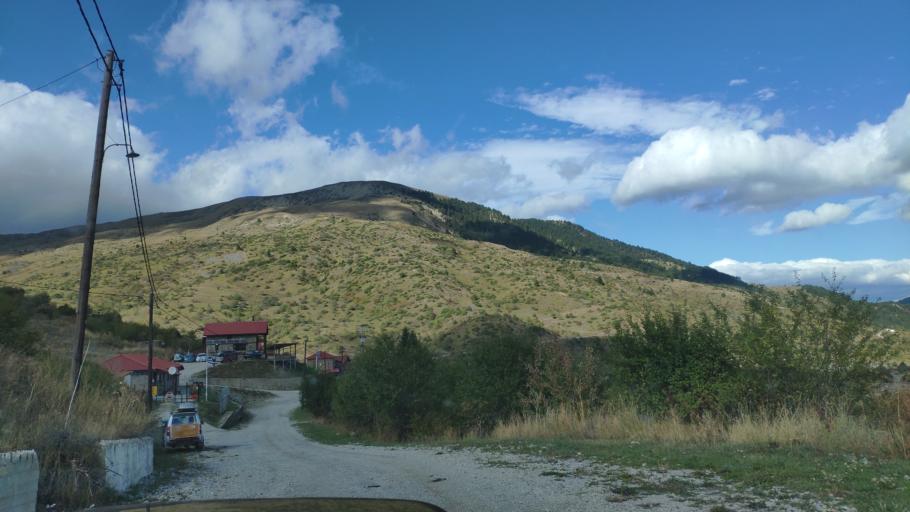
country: AL
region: Korce
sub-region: Rrethi i Devollit
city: Miras
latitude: 40.3923
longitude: 20.8362
